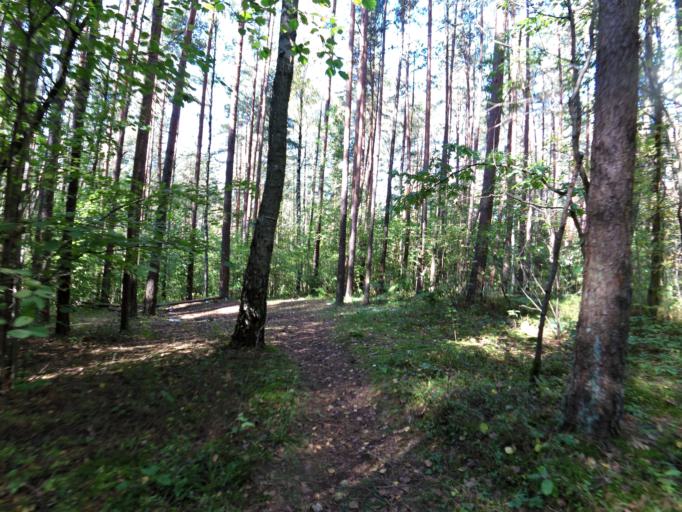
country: LT
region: Vilnius County
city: Pilaite
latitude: 54.6920
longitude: 25.1991
